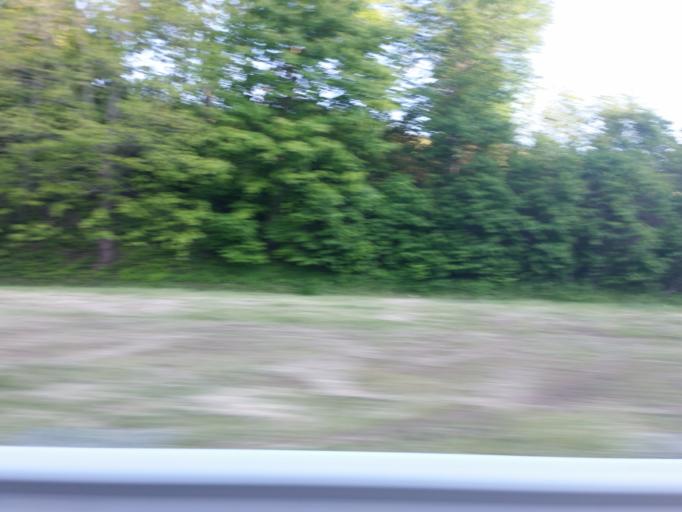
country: US
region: Virginia
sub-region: Russell County
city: Lebanon
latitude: 36.8517
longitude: -82.1213
